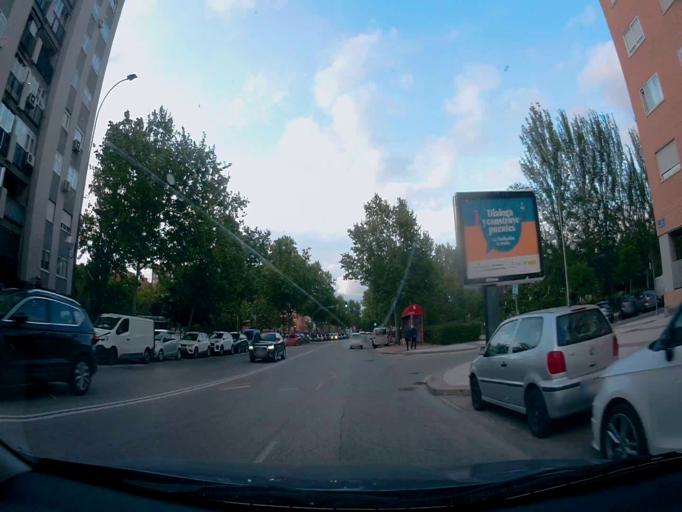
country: ES
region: Madrid
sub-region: Provincia de Madrid
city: Mostoles
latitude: 40.3269
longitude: -3.8826
